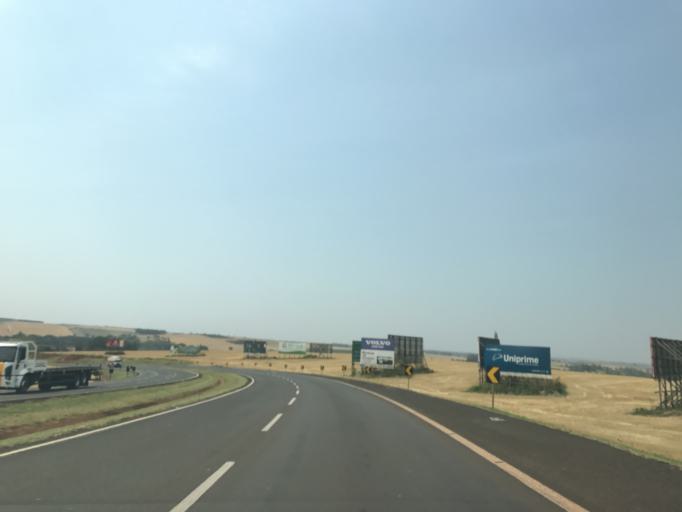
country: BR
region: Parana
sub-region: Rolandia
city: Rolandia
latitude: -23.3393
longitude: -51.3513
